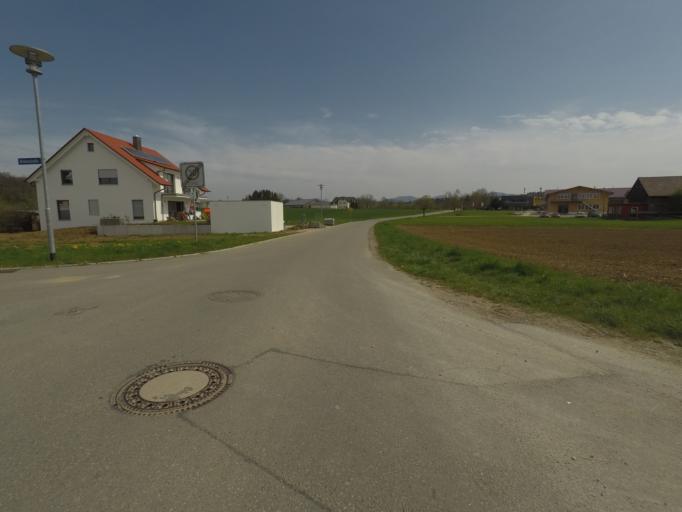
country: DE
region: Baden-Wuerttemberg
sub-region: Tuebingen Region
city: Wannweil
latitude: 48.5010
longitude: 9.1327
